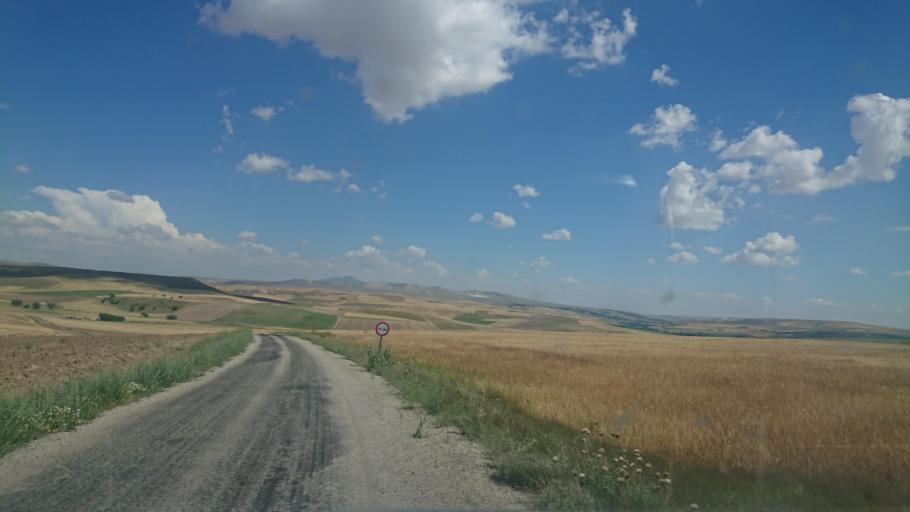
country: TR
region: Aksaray
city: Agacoren
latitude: 38.8021
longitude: 33.8132
